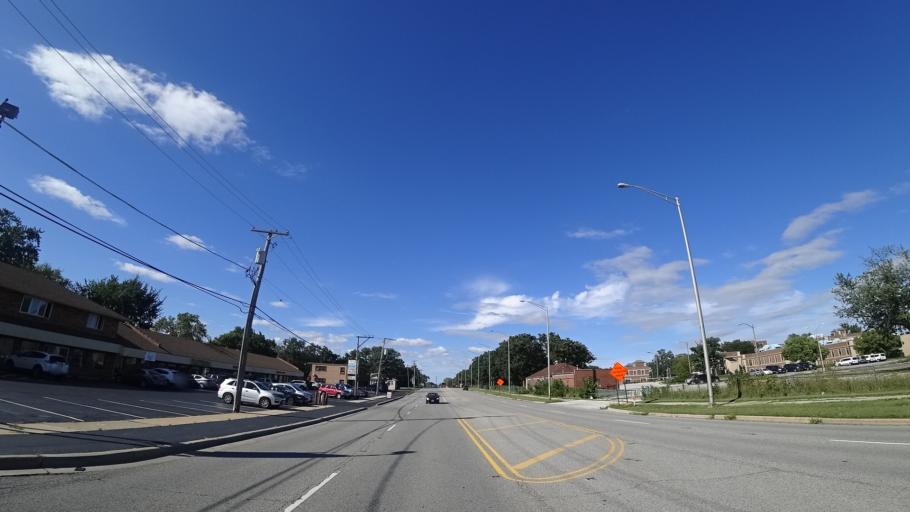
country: US
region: Illinois
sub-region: Cook County
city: Oak Forest
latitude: 41.5980
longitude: -87.7363
